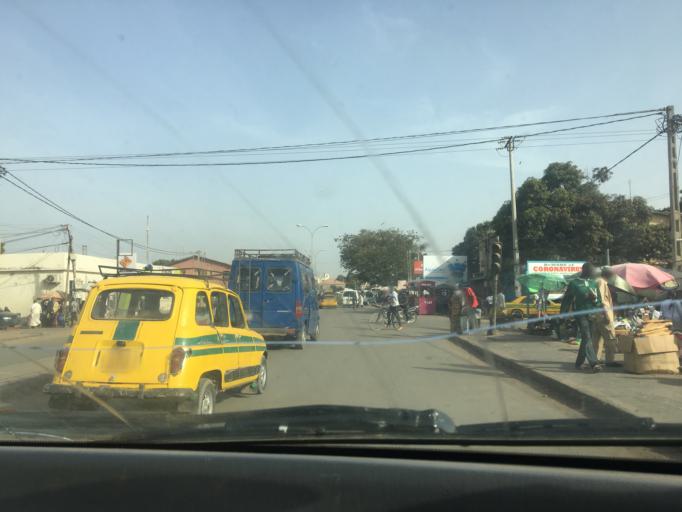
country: GM
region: Western
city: Abuko
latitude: 13.4133
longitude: -16.6715
